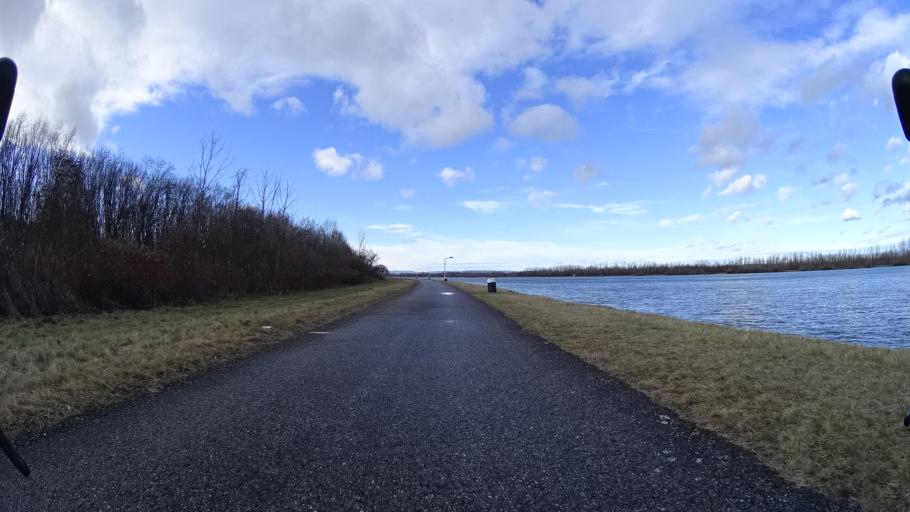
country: AT
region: Lower Austria
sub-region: Politischer Bezirk Tulln
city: Fels am Wagram
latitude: 48.3780
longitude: 15.8456
